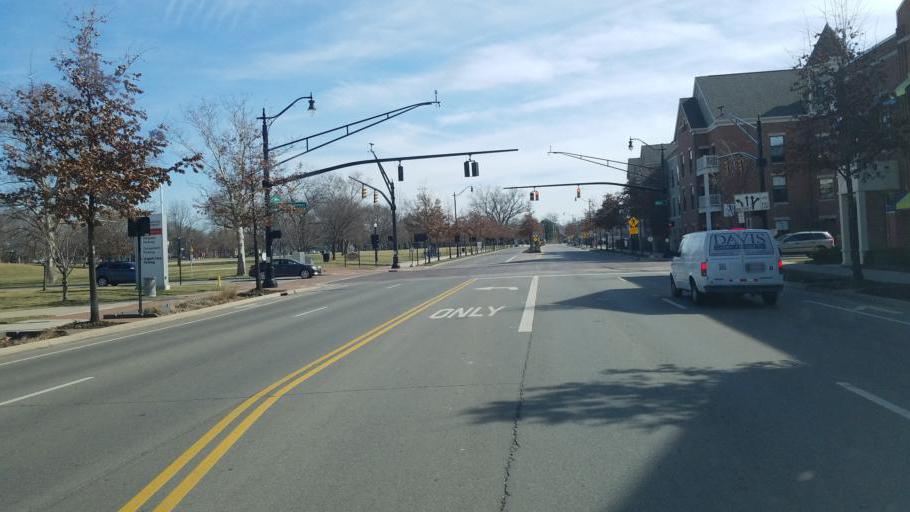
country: US
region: Ohio
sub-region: Franklin County
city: Columbus
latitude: 39.9516
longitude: -82.9803
